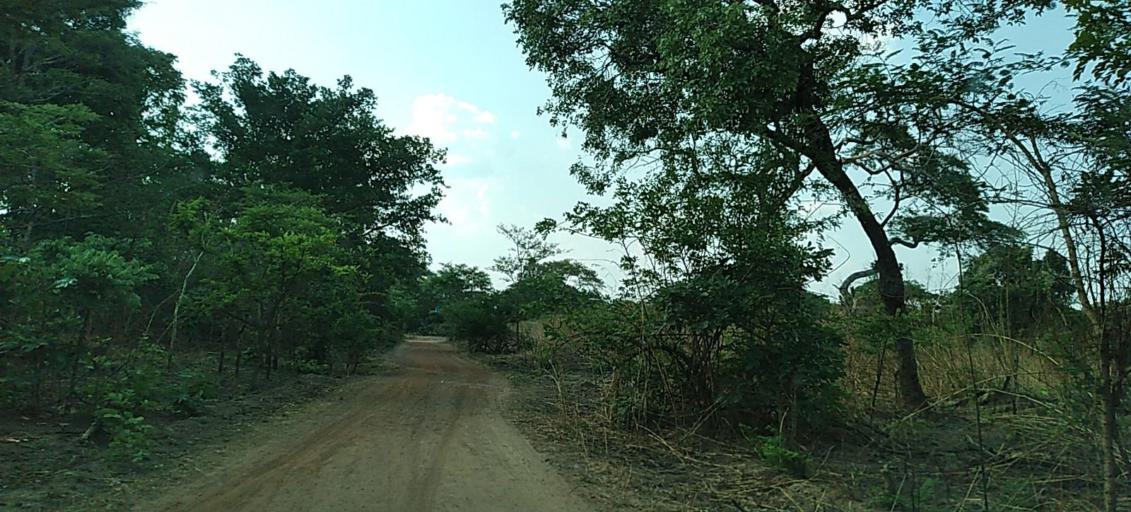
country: ZM
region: Copperbelt
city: Mpongwe
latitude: -13.4698
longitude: 28.0702
